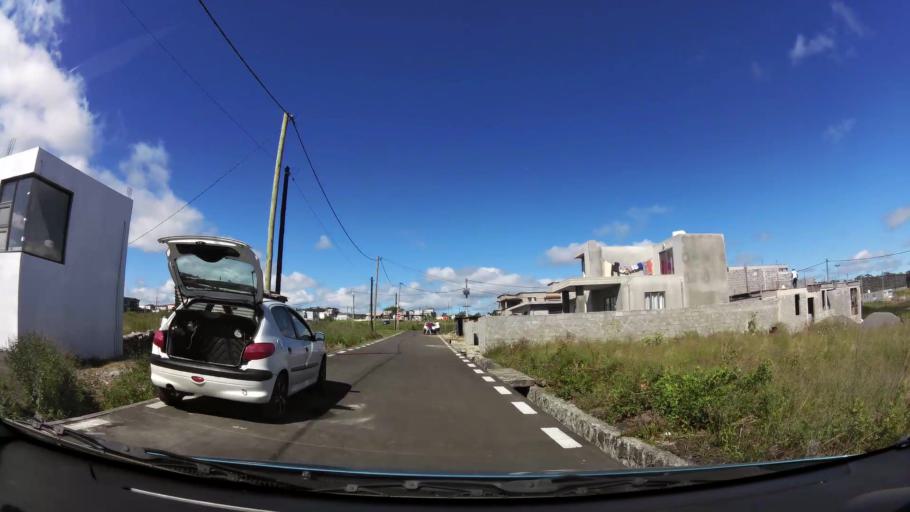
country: MU
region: Plaines Wilhems
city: Vacoas
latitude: -20.3350
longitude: 57.4801
